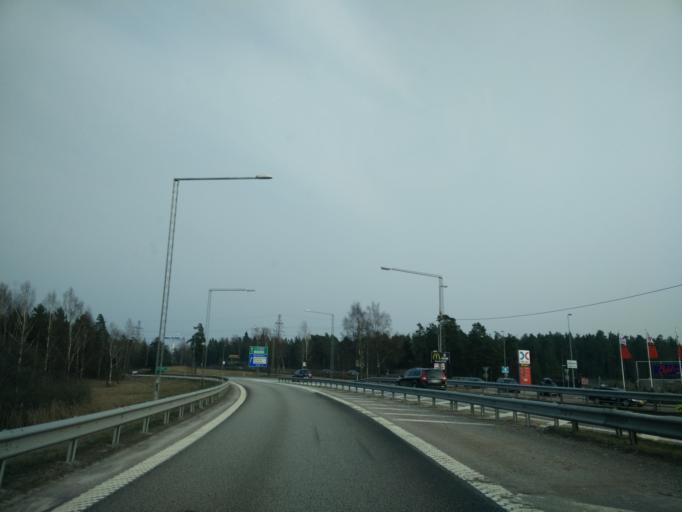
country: SE
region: Vaermland
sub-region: Hammaro Kommun
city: Skoghall
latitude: 59.3789
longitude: 13.4293
